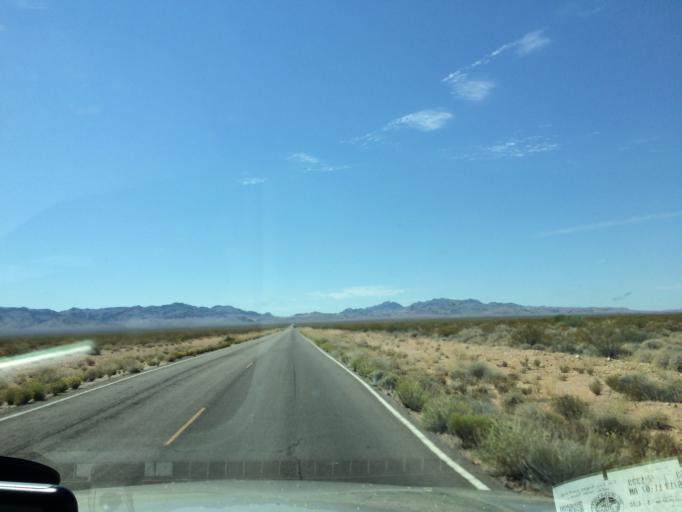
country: US
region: Nevada
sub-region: Clark County
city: Moapa Town
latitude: 36.4794
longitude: -114.7455
